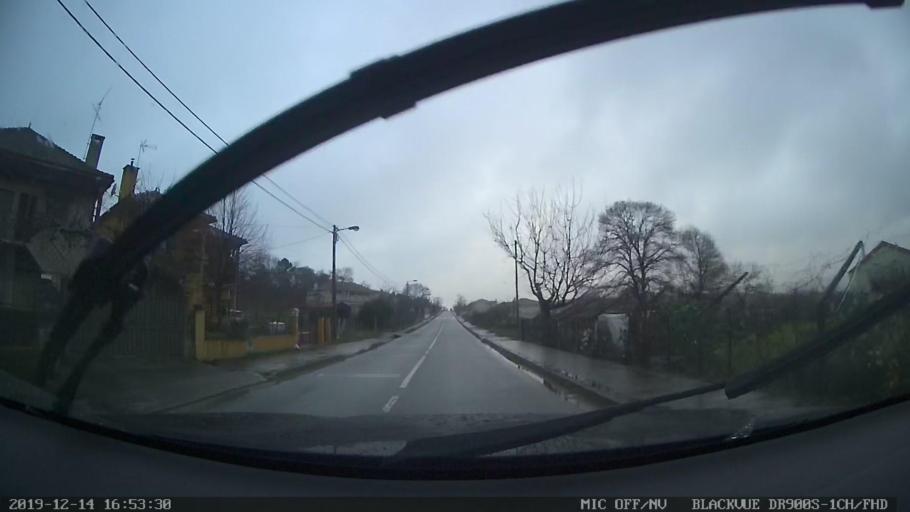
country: PT
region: Vila Real
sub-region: Murca
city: Murca
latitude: 41.4314
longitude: -7.5172
